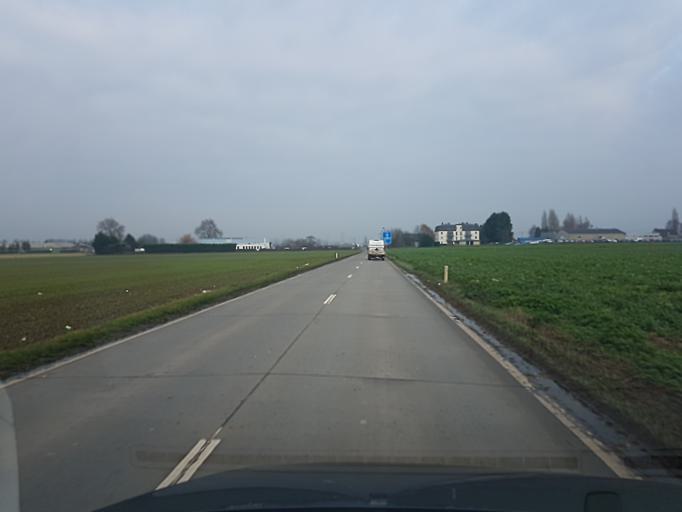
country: BE
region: Wallonia
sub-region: Province de Liege
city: Hannut
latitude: 50.6819
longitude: 5.0611
